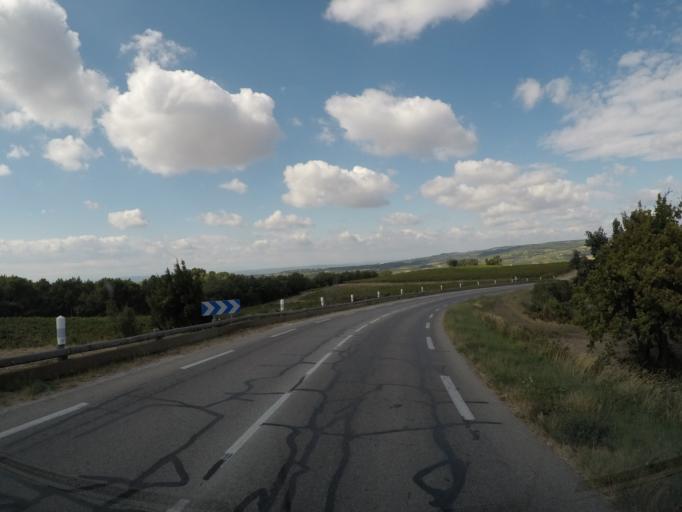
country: FR
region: Provence-Alpes-Cote d'Azur
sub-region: Departement du Vaucluse
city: Visan
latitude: 44.2751
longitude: 4.9995
